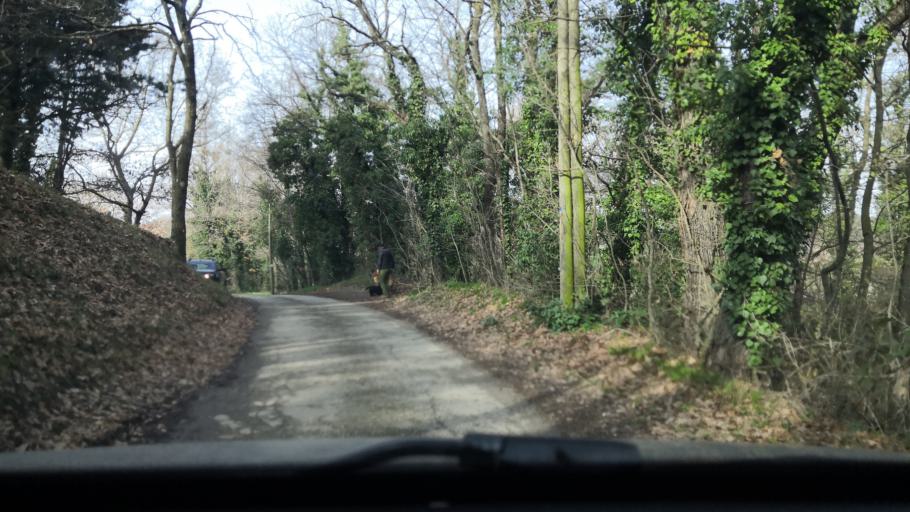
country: FR
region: Rhone-Alpes
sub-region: Departement de la Drome
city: La Begude-de-Mazenc
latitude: 44.5385
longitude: 4.9420
